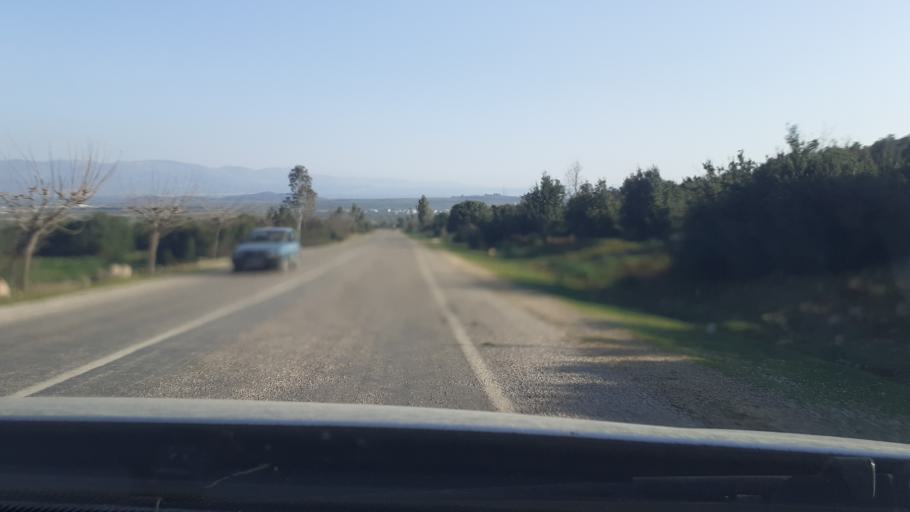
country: TR
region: Hatay
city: Aktepe
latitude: 36.7285
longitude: 36.4827
